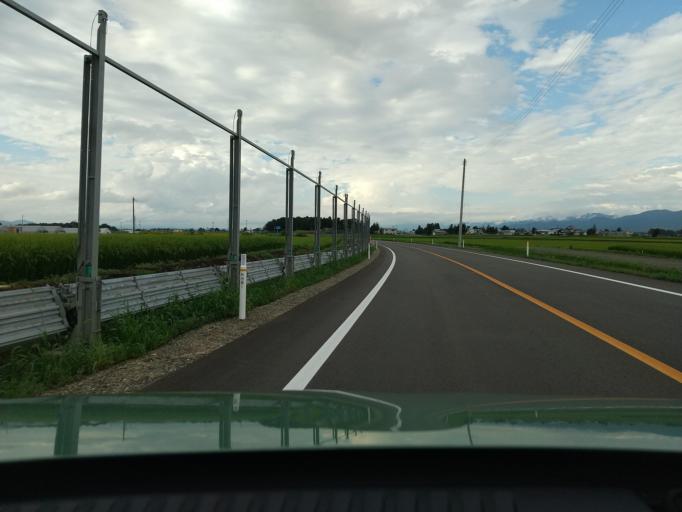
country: JP
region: Akita
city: Yokotemachi
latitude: 39.2966
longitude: 140.4856
